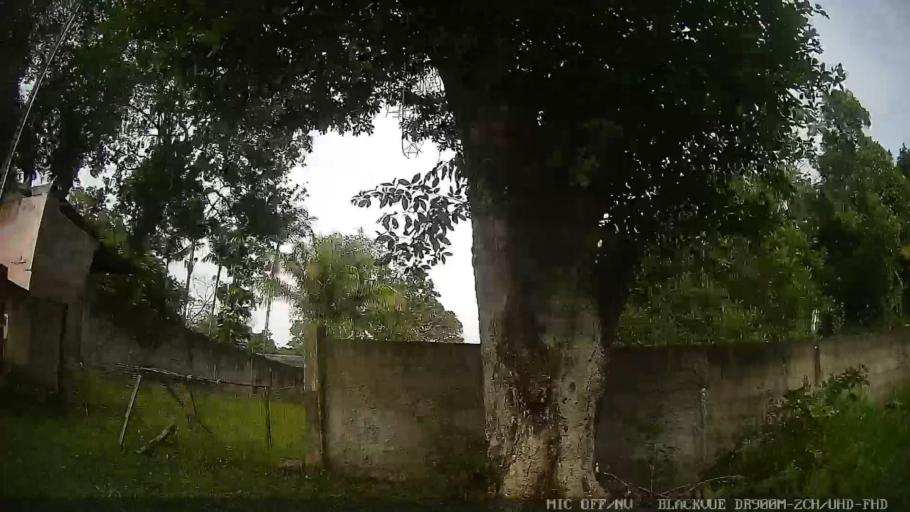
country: BR
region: Sao Paulo
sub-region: Peruibe
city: Peruibe
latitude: -24.2245
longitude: -46.9248
